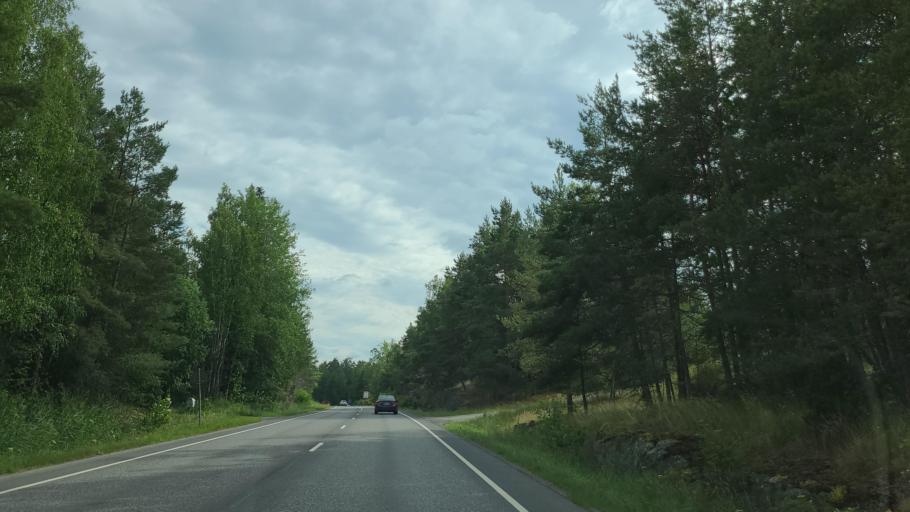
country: FI
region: Varsinais-Suomi
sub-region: Turku
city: Rymaettylae
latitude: 60.4202
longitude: 21.8967
